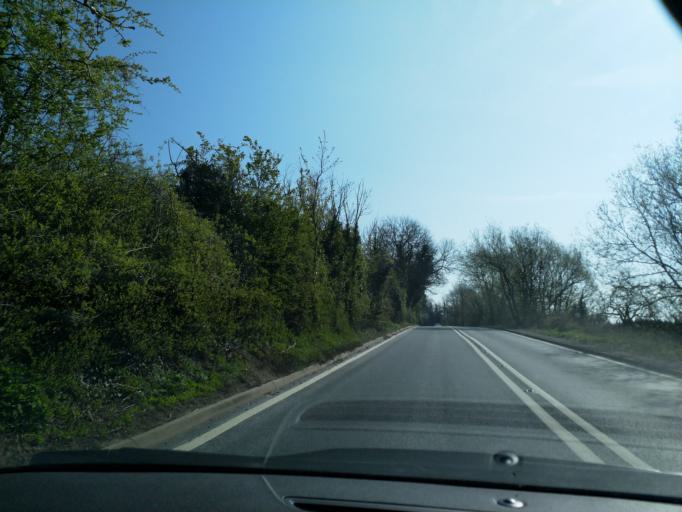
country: GB
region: England
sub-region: Warwickshire
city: Stratford-upon-Avon
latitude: 52.1844
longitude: -1.7448
